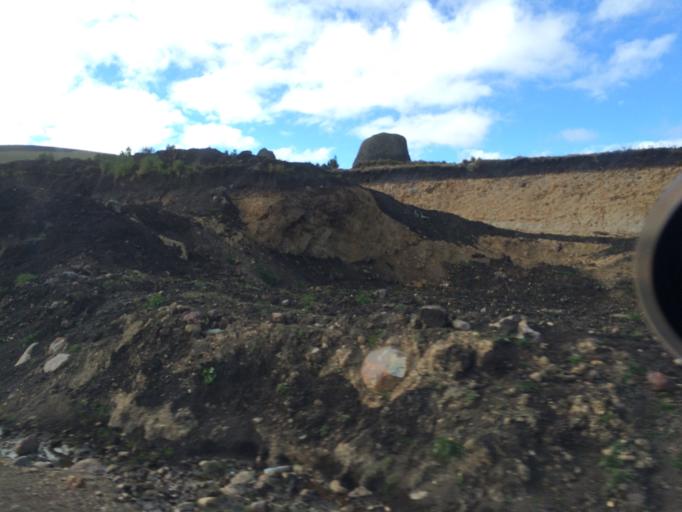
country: EC
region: Chimborazo
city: Alausi
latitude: -2.2490
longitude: -78.6624
